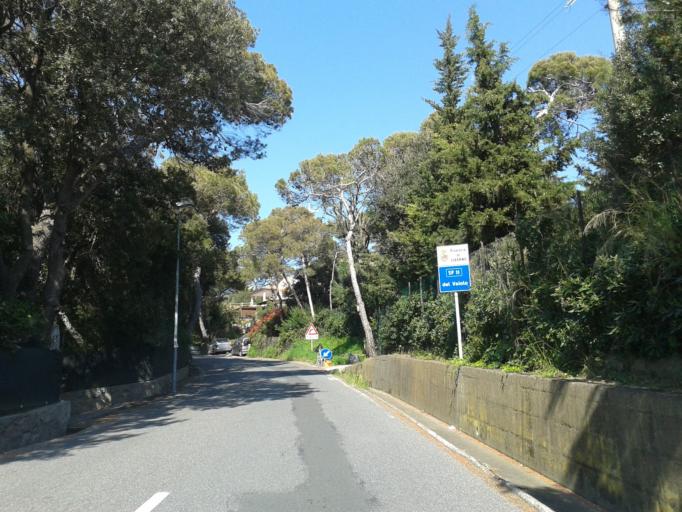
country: IT
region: Tuscany
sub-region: Provincia di Livorno
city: Quercianella
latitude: 43.4482
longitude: 10.3815
